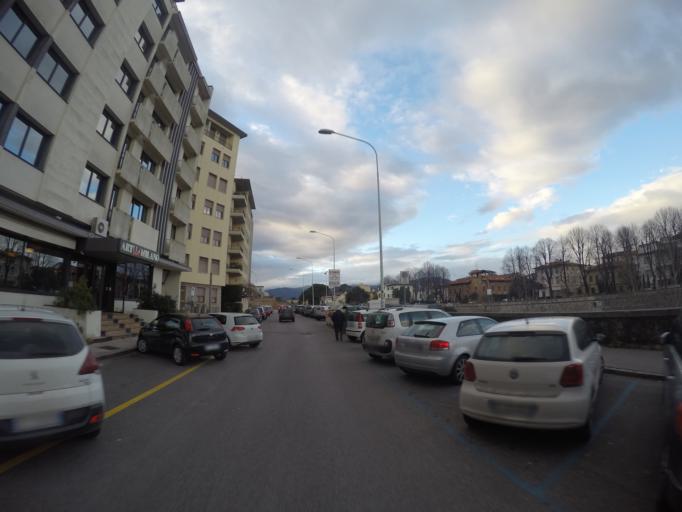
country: IT
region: Tuscany
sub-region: Provincia di Prato
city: Prato
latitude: 43.8783
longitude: 11.1055
